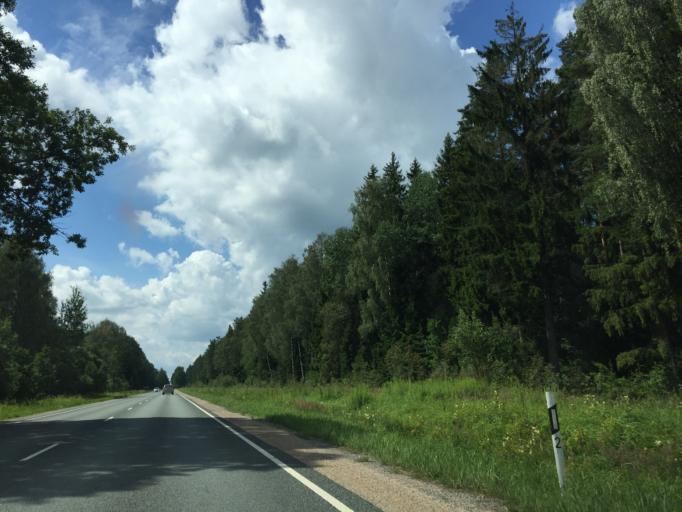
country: LV
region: Ozolnieku
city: Ozolnieki
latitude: 56.7130
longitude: 23.8315
